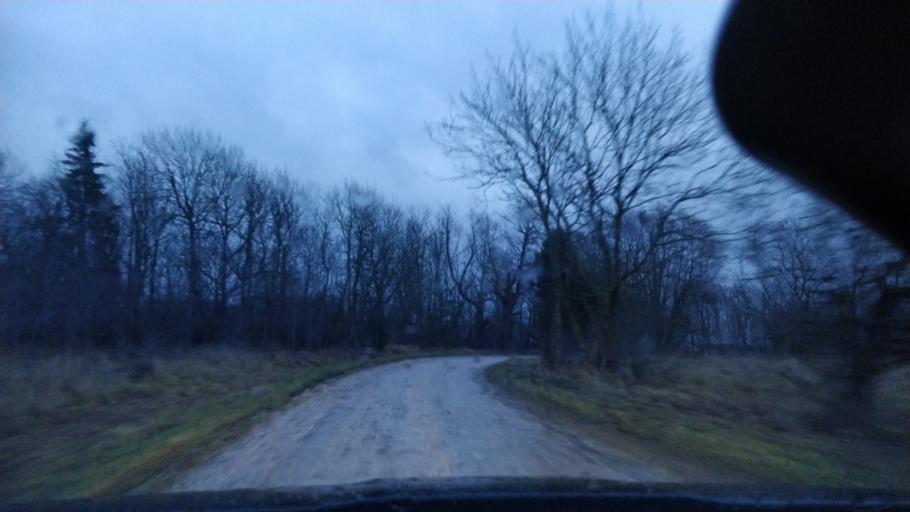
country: EE
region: Laeaene
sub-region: Lihula vald
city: Lihula
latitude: 58.8496
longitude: 23.9823
